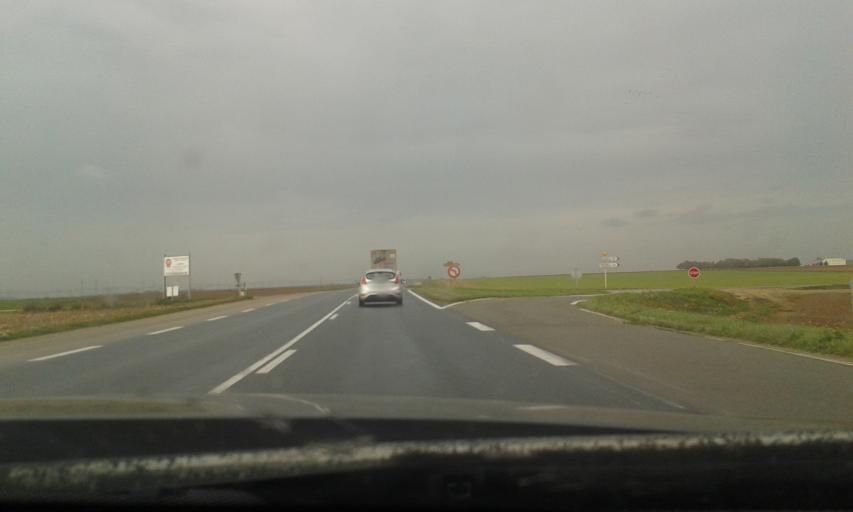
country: FR
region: Centre
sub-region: Departement d'Eure-et-Loir
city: Janville
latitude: 48.2377
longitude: 1.7837
